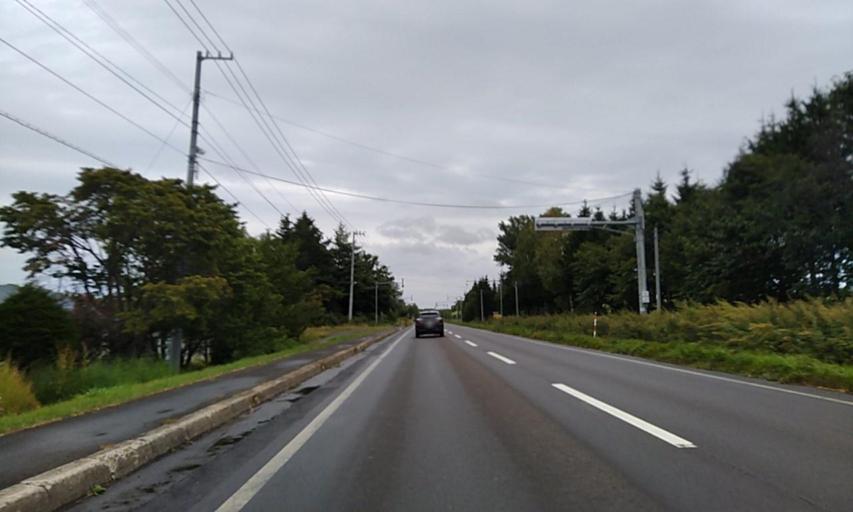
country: JP
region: Hokkaido
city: Kitami
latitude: 44.0843
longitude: 143.9484
